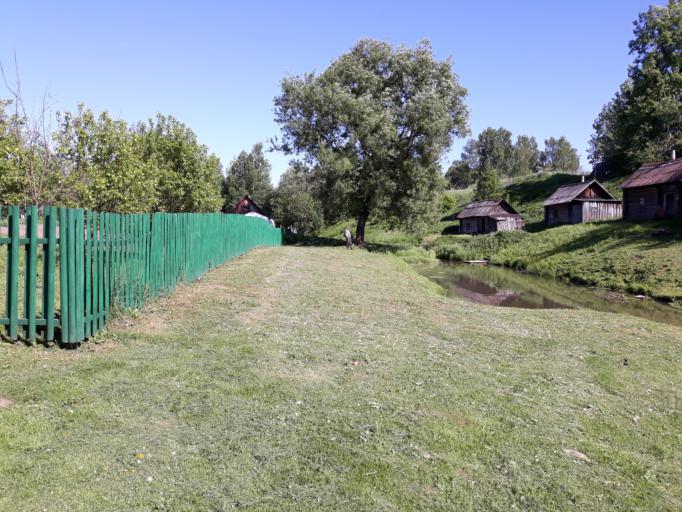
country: RU
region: Jaroslavl
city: Krasnyy Profintern
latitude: 57.8651
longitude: 40.2694
